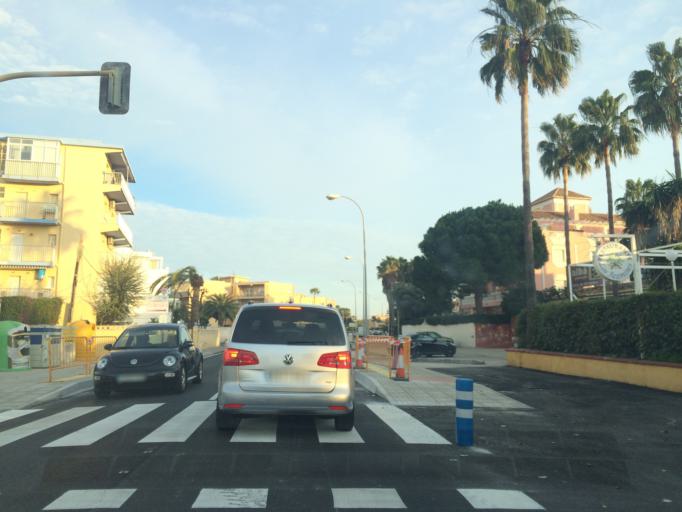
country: ES
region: Valencia
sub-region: Provincia de Alicante
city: els Poblets
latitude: 38.8580
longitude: 0.0637
